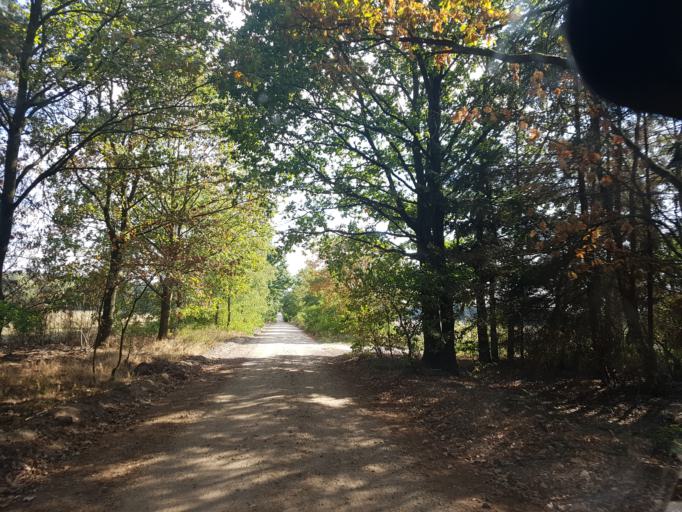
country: DE
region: Brandenburg
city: Gorzke
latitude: 52.0426
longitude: 12.2941
